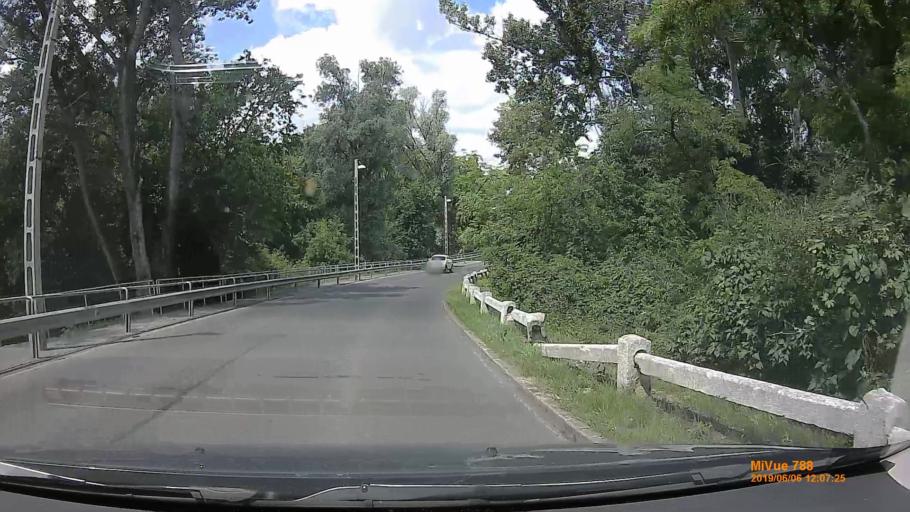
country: HU
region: Pest
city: Kerepes
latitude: 47.5648
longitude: 19.2714
